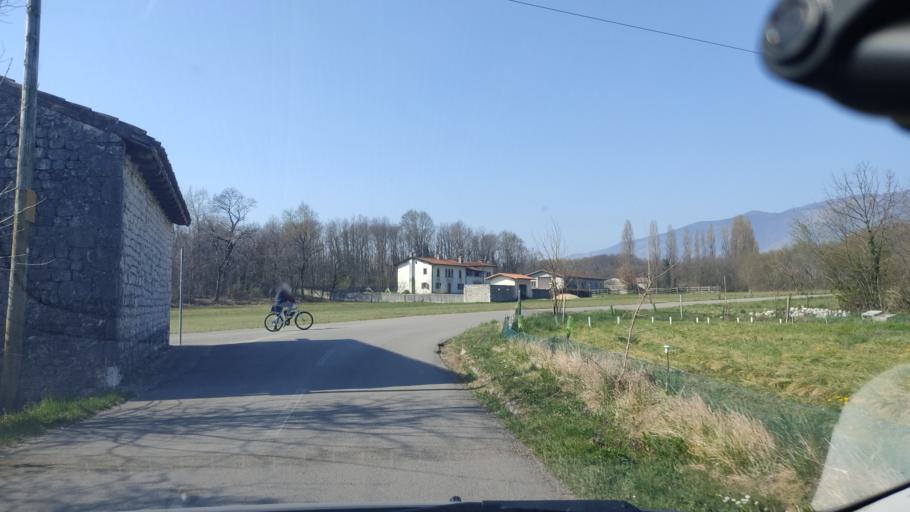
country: IT
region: Friuli Venezia Giulia
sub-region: Provincia di Pordenone
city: Budoia
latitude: 46.0497
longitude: 12.5491
